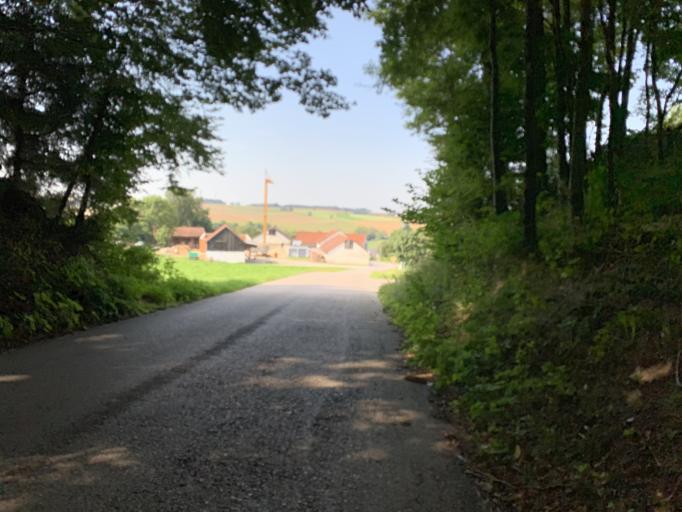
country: DE
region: Bavaria
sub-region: Upper Bavaria
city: Langenbach
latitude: 48.4209
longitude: 11.8328
